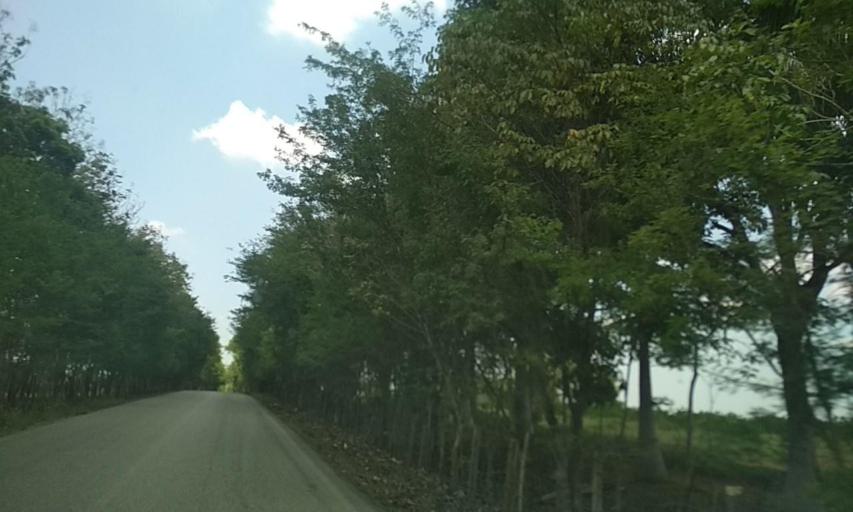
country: MX
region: Tabasco
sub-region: Huimanguillo
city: Paso de la Mina 2da. Seccion (Barrial)
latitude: 17.7733
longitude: -93.6432
